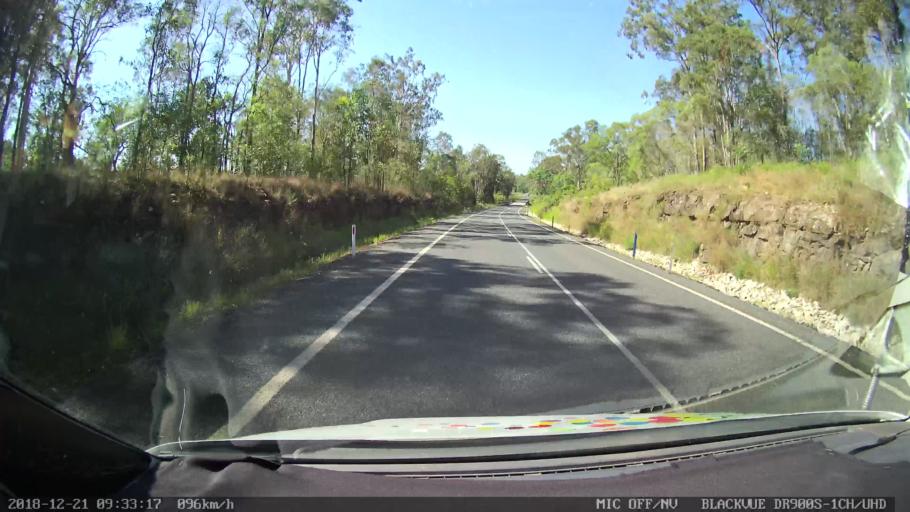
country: AU
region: New South Wales
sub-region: Clarence Valley
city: Grafton
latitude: -29.4822
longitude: 152.9768
